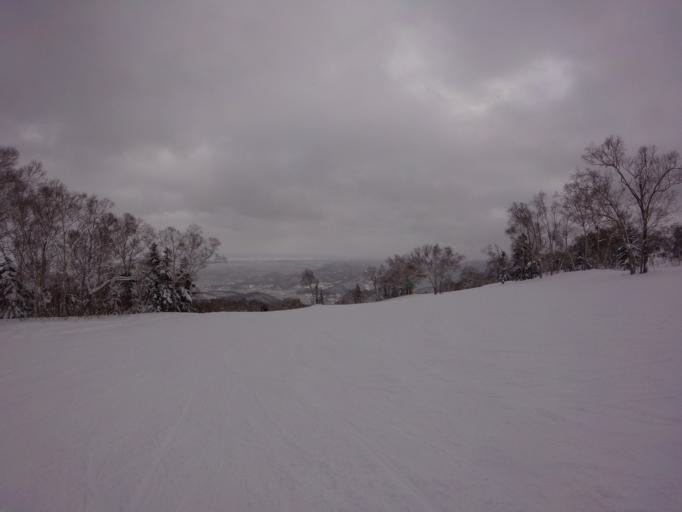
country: JP
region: Hokkaido
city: Sapporo
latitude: 43.0736
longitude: 141.2003
